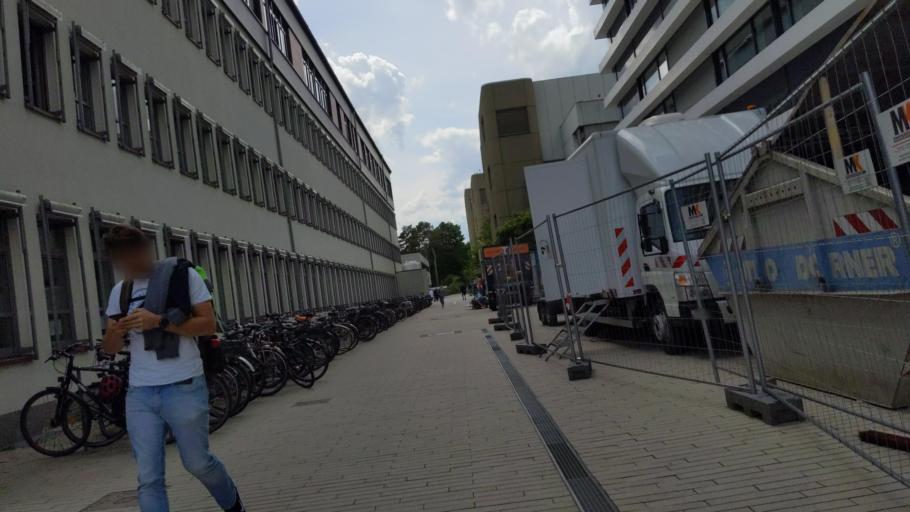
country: DE
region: Schleswig-Holstein
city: Luebeck
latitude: 53.8345
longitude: 10.7040
